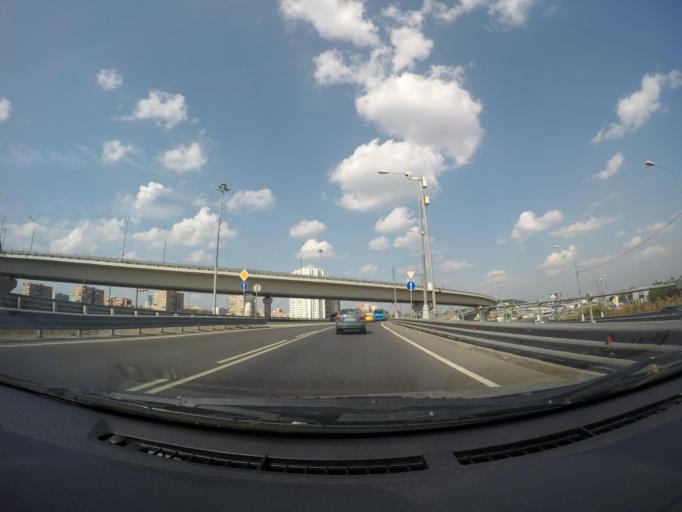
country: RU
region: Moskovskaya
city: Levoberezhnaya
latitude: 55.8855
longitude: 37.4825
